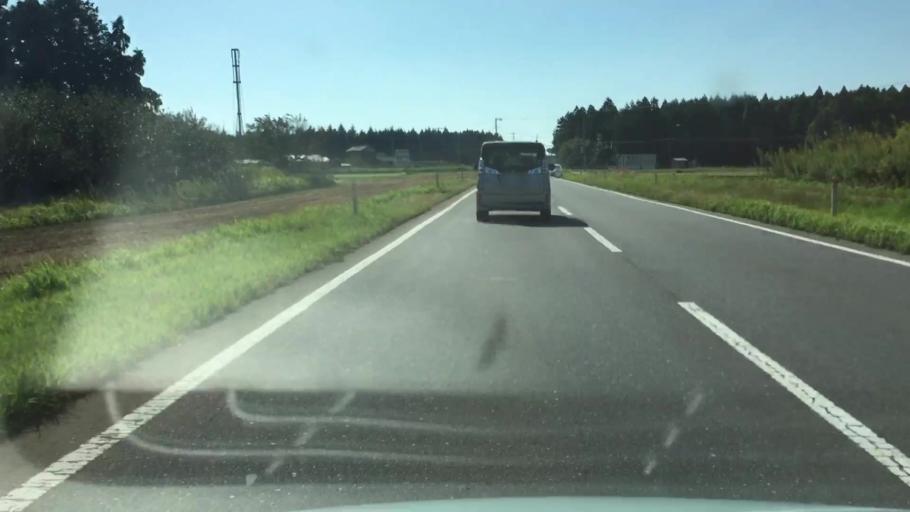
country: JP
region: Ibaraki
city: Ami
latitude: 35.9858
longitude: 140.1854
